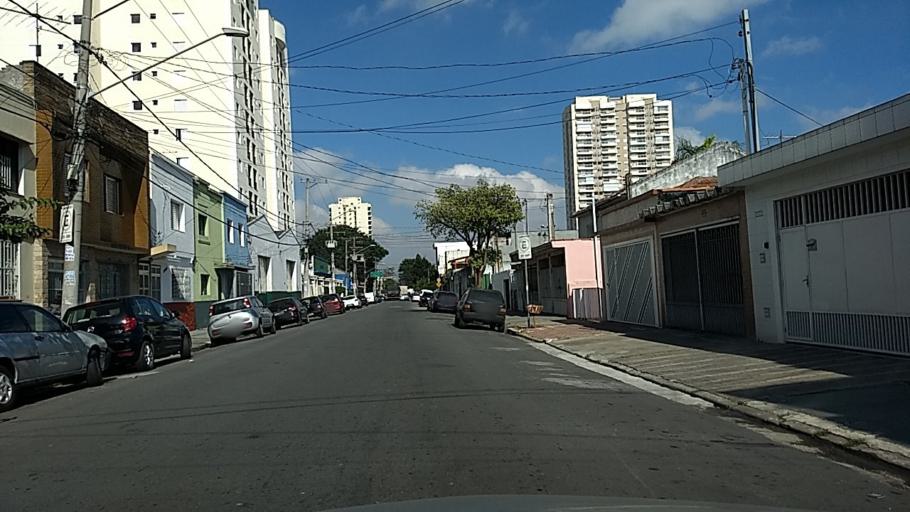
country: BR
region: Sao Paulo
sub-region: Sao Paulo
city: Sao Paulo
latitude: -23.5177
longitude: -46.5863
